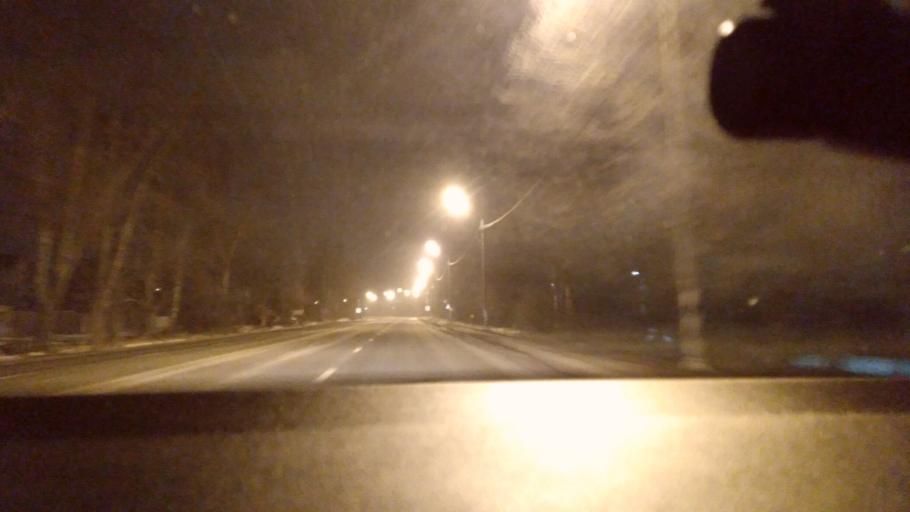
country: RU
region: Moskovskaya
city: Bronnitsy
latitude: 55.4650
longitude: 38.2003
